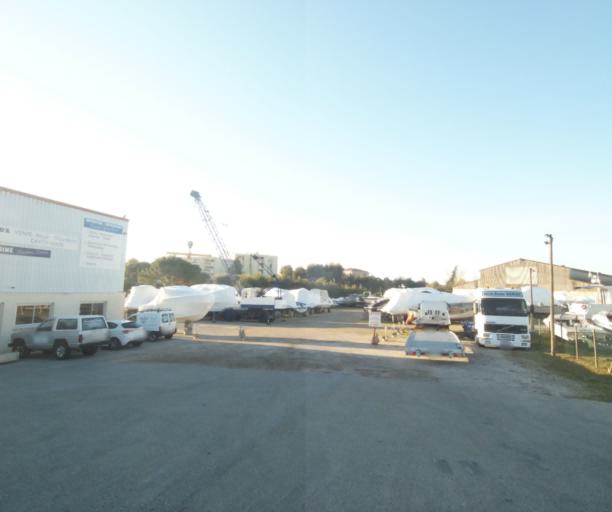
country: FR
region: Provence-Alpes-Cote d'Azur
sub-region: Departement des Alpes-Maritimes
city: Vallauris
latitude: 43.5754
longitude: 7.0801
